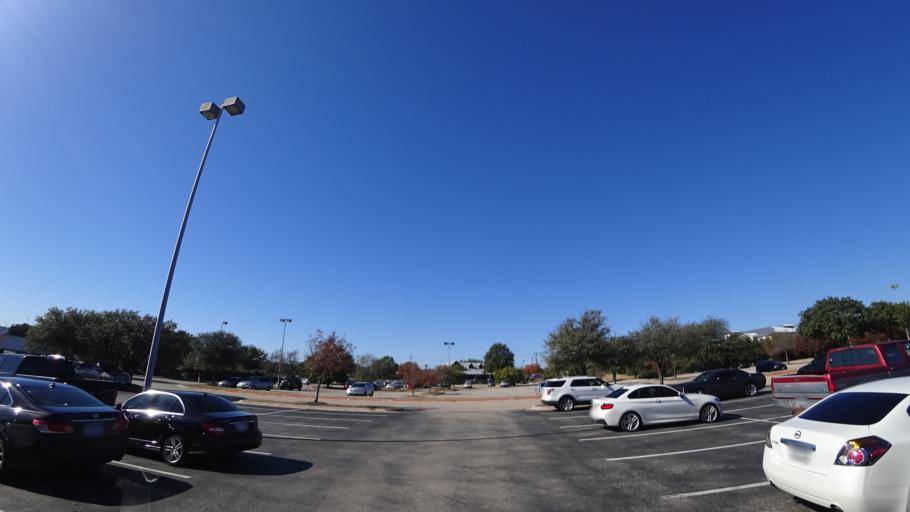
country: US
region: Texas
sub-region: Travis County
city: Wells Branch
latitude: 30.4232
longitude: -97.7008
